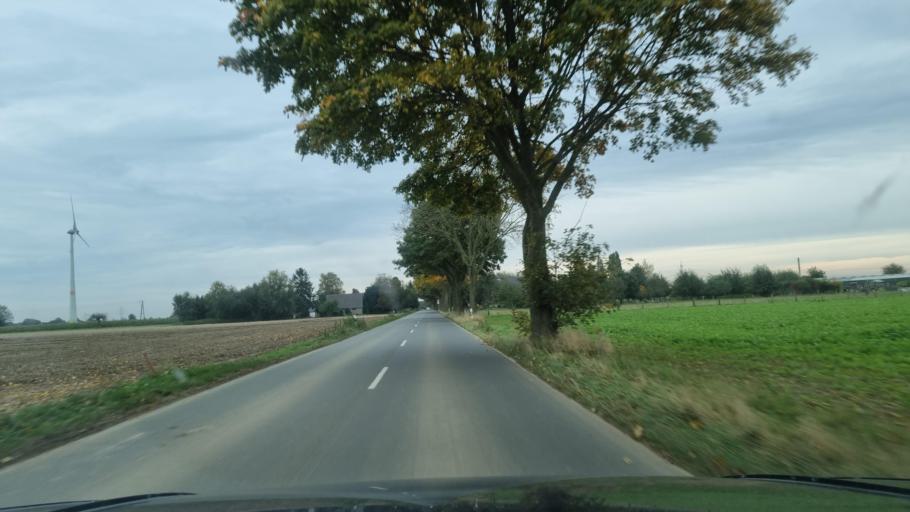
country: DE
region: North Rhine-Westphalia
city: Kalkar
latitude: 51.7154
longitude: 6.2761
